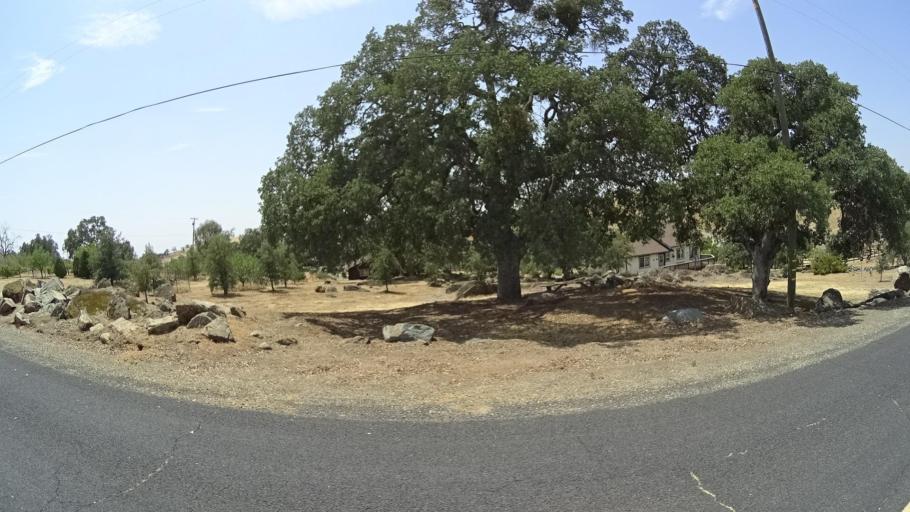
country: US
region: California
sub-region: Tuolumne County
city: Jamestown
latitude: 37.6442
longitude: -120.3273
